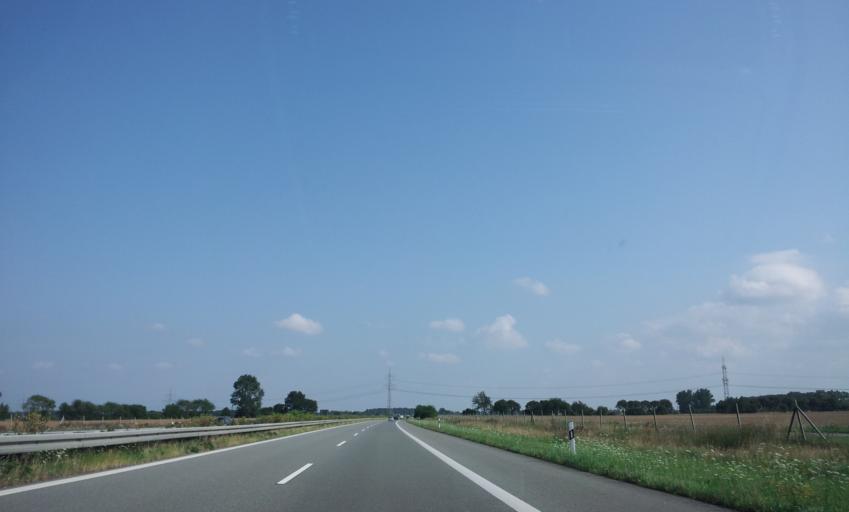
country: DE
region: Mecklenburg-Vorpommern
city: Dersekow
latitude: 54.0461
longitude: 13.2595
